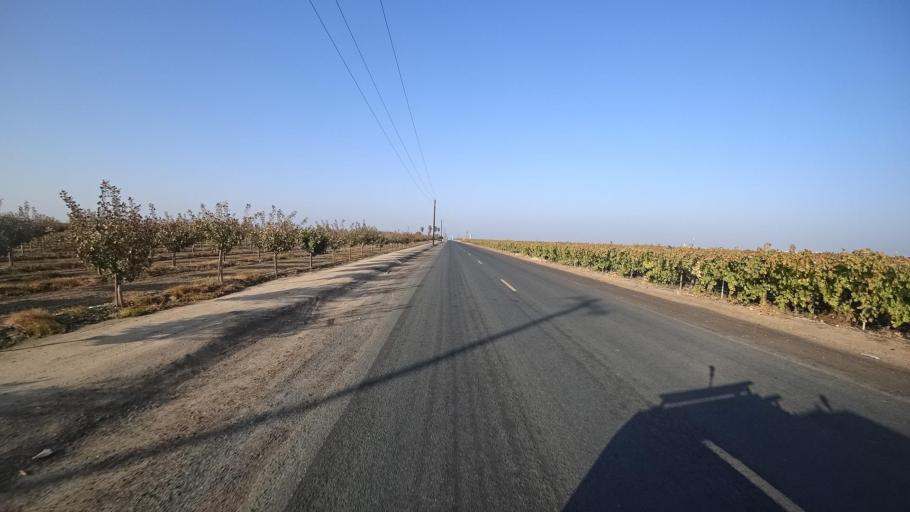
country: US
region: California
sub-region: Tulare County
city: Richgrove
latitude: 35.7906
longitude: -119.1388
